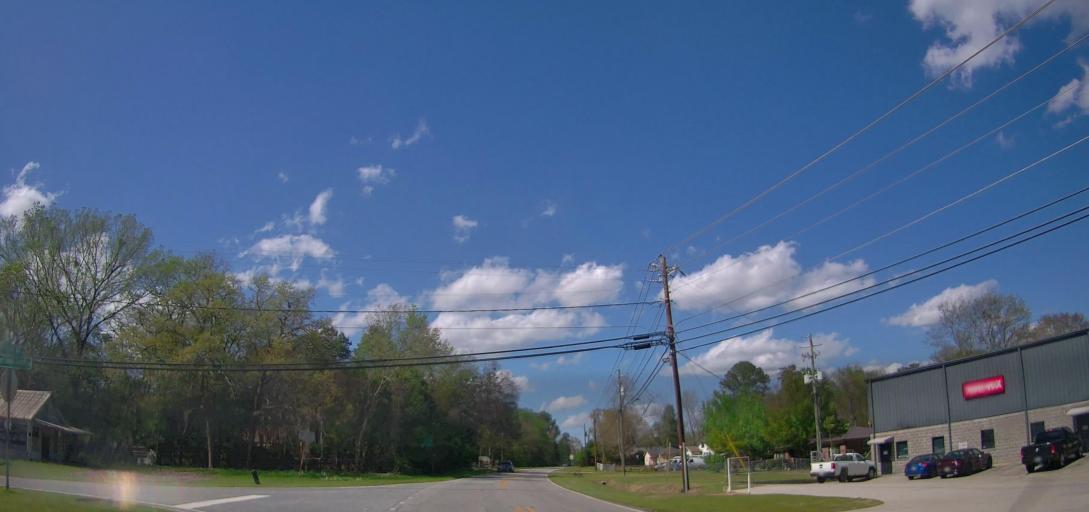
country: US
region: Georgia
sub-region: Bibb County
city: Macon
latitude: 32.8294
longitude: -83.5618
